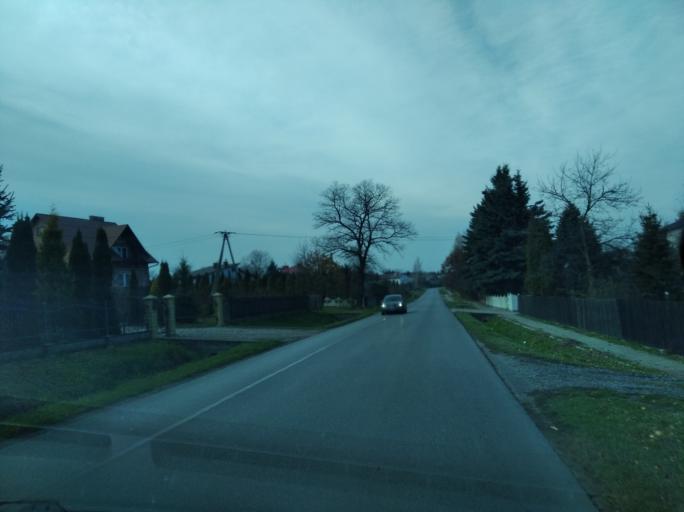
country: PL
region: Subcarpathian Voivodeship
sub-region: Powiat ropczycko-sedziszowski
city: Iwierzyce
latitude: 50.0551
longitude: 21.7413
